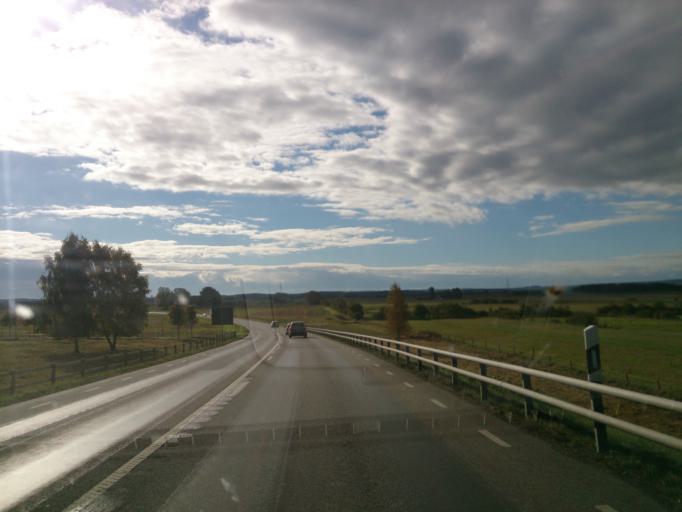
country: SE
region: Skane
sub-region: Sjobo Kommun
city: Sjoebo
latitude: 55.6319
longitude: 13.6815
